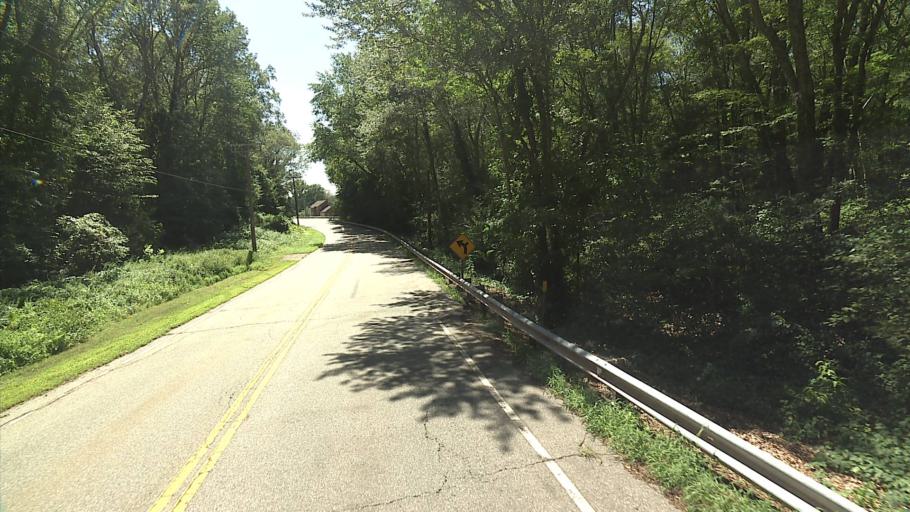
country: US
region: Connecticut
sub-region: New London County
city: Baltic
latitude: 41.6583
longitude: -72.0913
